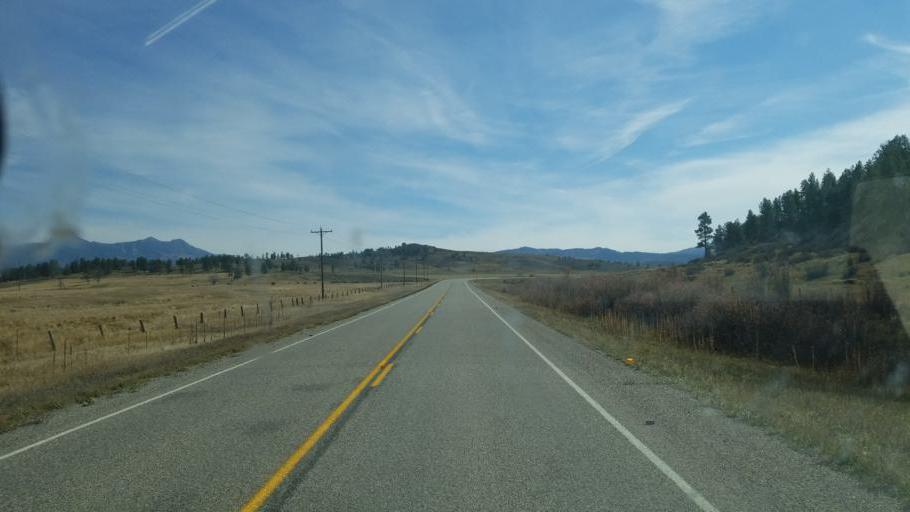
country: US
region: New Mexico
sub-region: Rio Arriba County
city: Dulce
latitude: 37.0341
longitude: -106.8358
